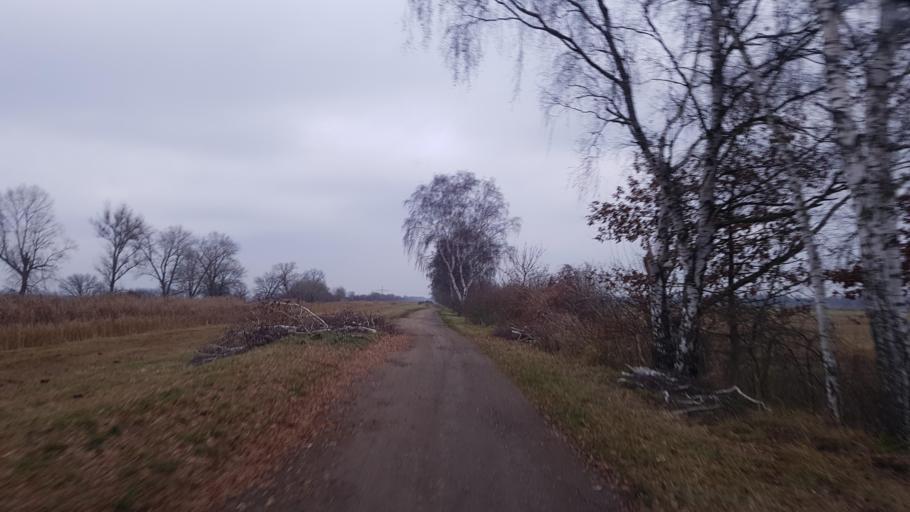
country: DE
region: Brandenburg
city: Plessa
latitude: 51.4621
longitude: 13.6576
